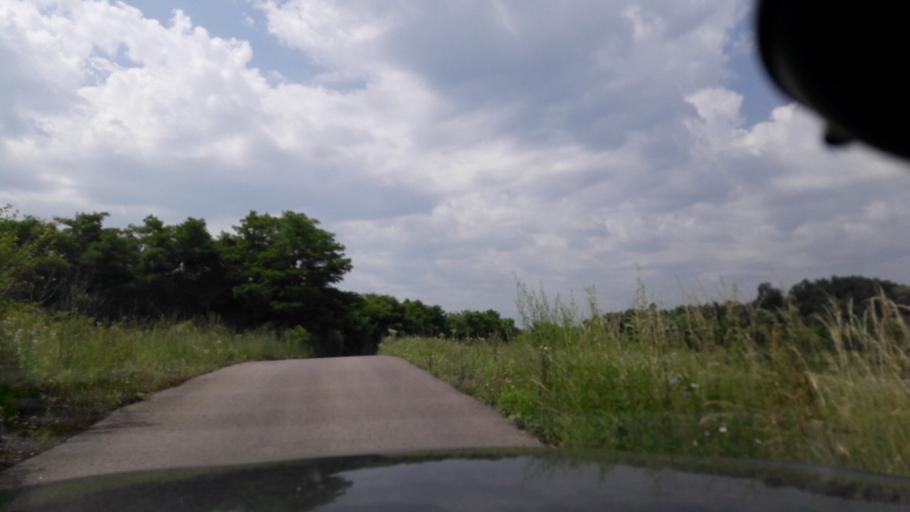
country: RS
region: Central Serbia
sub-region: Belgrade
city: Sopot
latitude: 44.6161
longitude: 20.5996
